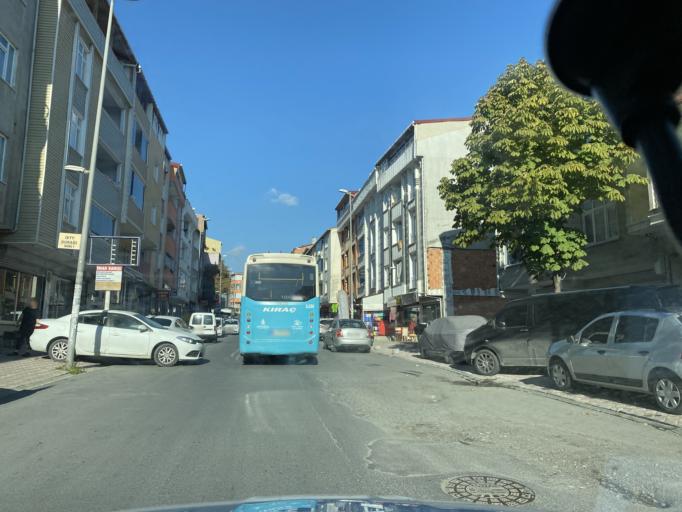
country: TR
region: Istanbul
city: Esenyurt
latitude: 41.0312
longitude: 28.6529
